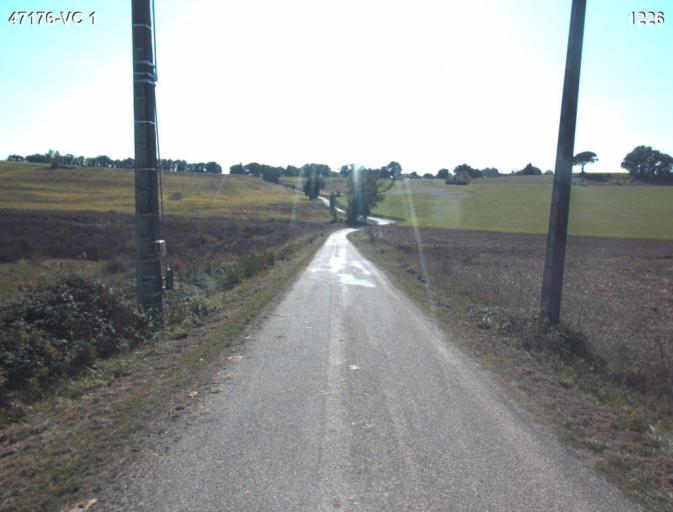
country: FR
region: Aquitaine
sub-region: Departement du Lot-et-Garonne
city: Lavardac
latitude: 44.2035
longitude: 0.2936
